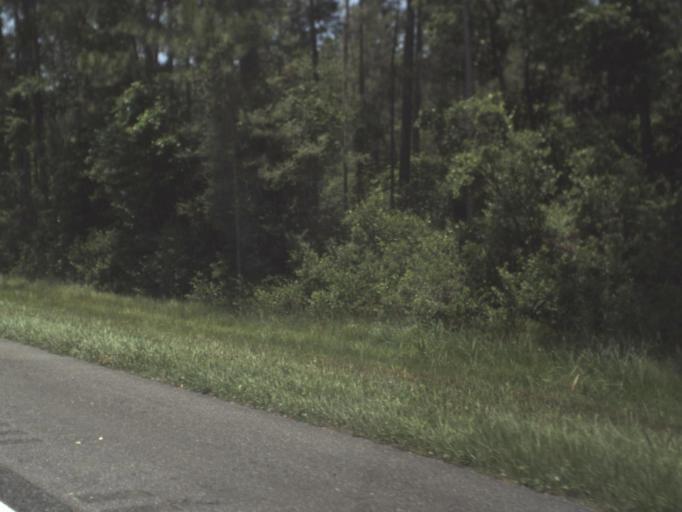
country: US
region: Florida
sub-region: Columbia County
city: Watertown
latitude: 30.2552
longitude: -82.4379
